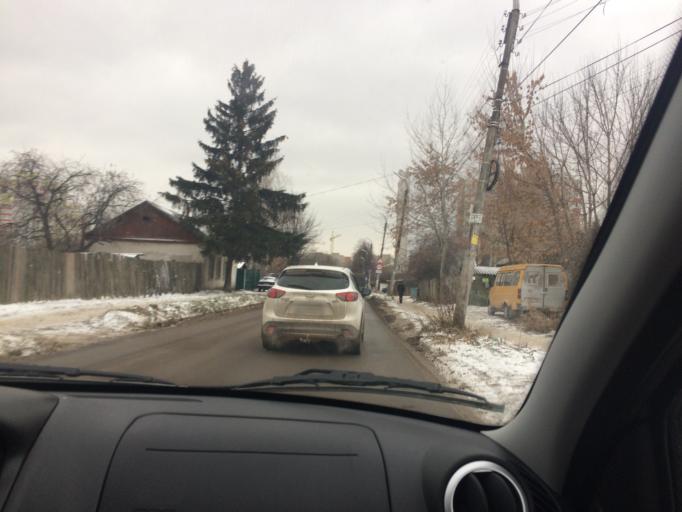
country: RU
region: Rjazan
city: Ryazan'
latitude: 54.6175
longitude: 39.7154
